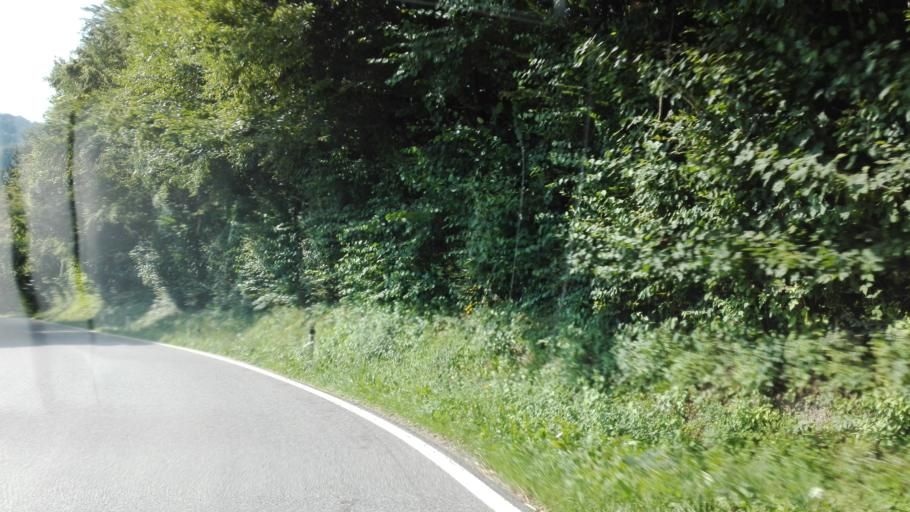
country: AT
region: Lower Austria
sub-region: Politischer Bezirk Sankt Polten
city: Rabenstein an der Pielach
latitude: 48.0363
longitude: 15.4913
